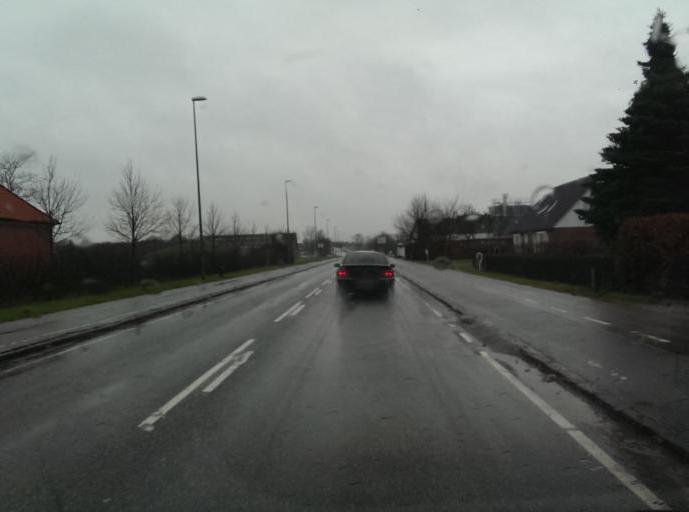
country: DK
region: South Denmark
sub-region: Varde Kommune
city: Olgod
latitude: 55.7191
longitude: 8.6114
